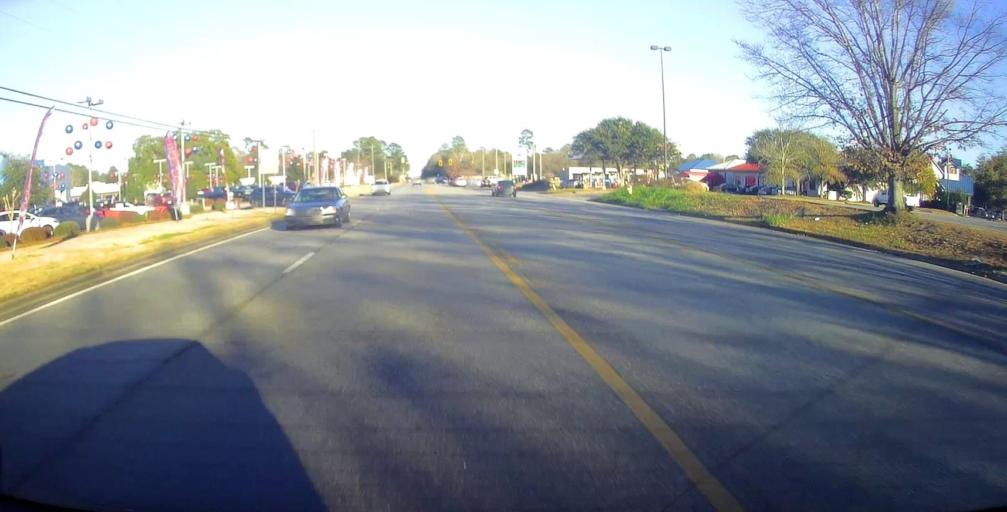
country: US
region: Georgia
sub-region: Dougherty County
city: Albany
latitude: 31.6226
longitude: -84.2059
